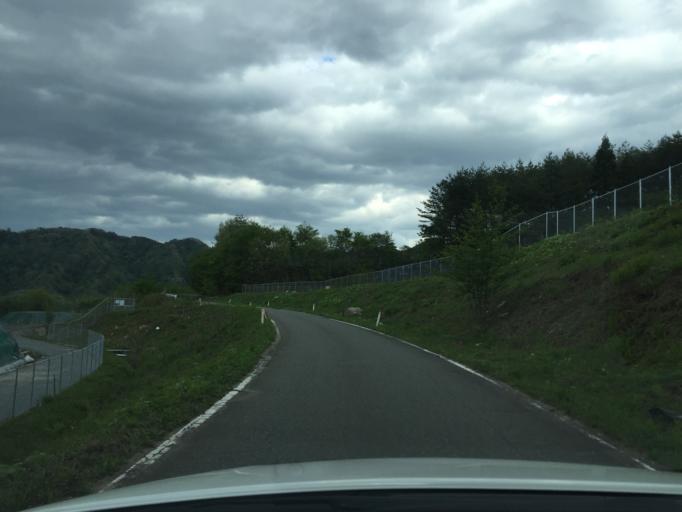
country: JP
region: Miyagi
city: Marumori
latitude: 37.7198
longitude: 140.8193
